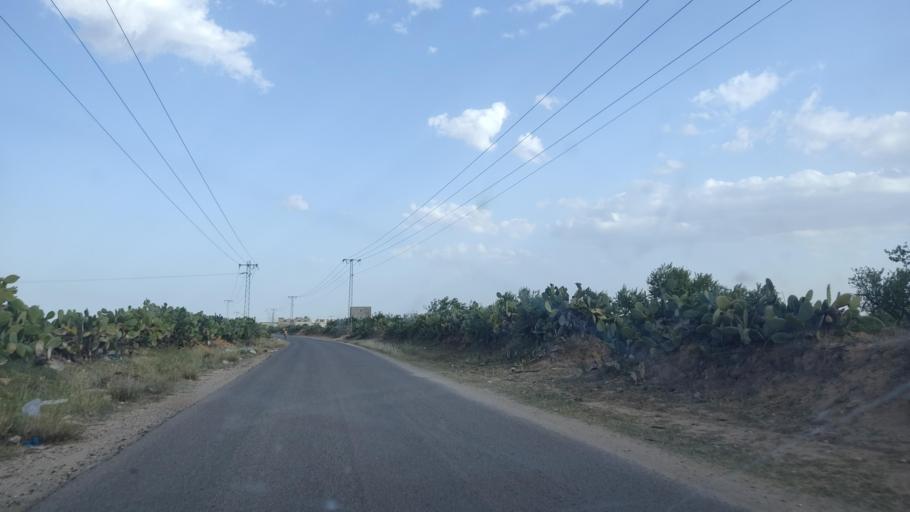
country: TN
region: Safaqis
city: Sfax
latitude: 34.8527
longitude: 10.6095
